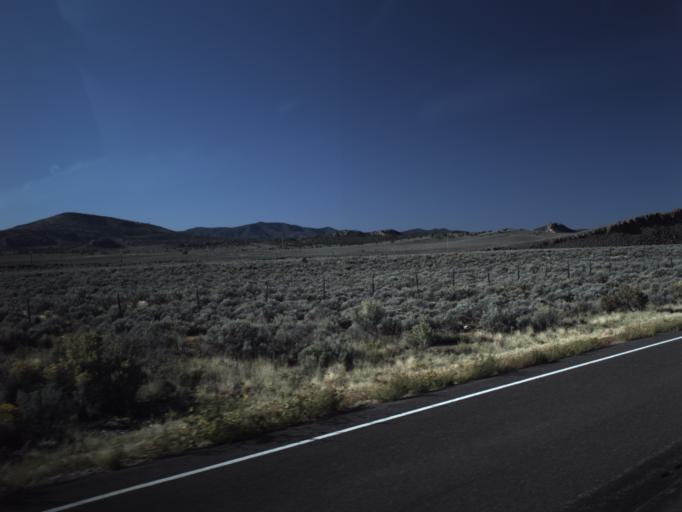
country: US
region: Utah
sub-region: Washington County
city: Enterprise
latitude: 37.7950
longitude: -113.9412
